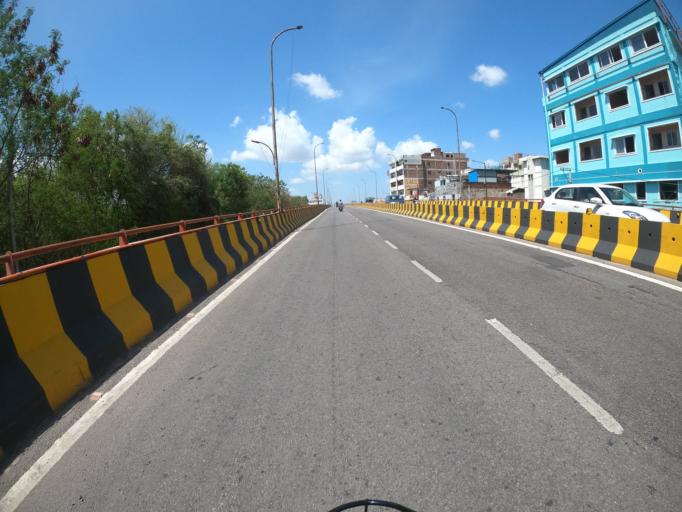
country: IN
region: Telangana
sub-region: Hyderabad
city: Hyderabad
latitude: 17.3799
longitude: 78.4214
